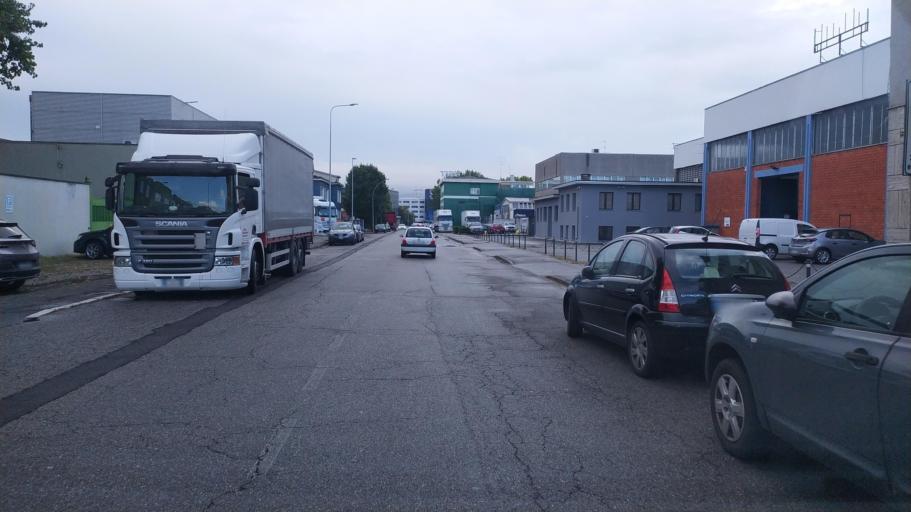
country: IT
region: Lombardy
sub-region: Citta metropolitana di Milano
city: Trezzano sul Naviglio
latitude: 45.4299
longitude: 9.0698
